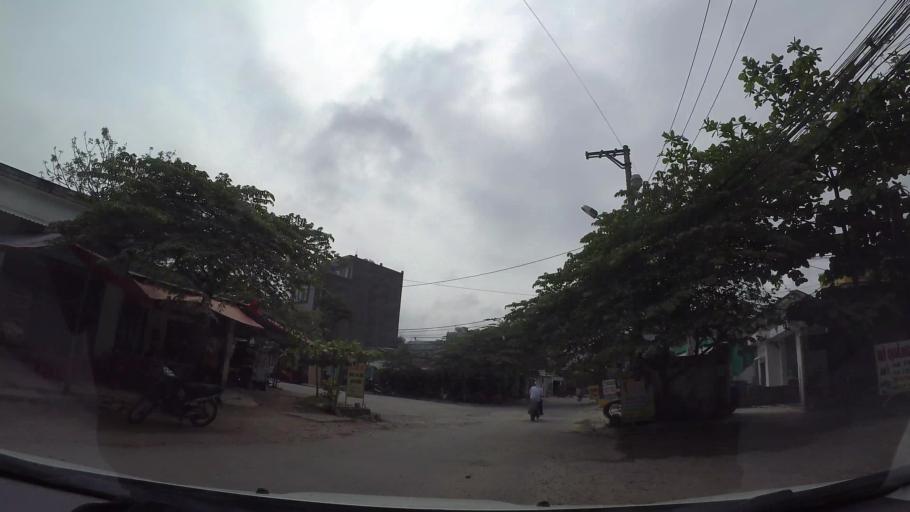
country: VN
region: Da Nang
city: Son Tra
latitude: 16.0894
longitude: 108.2446
